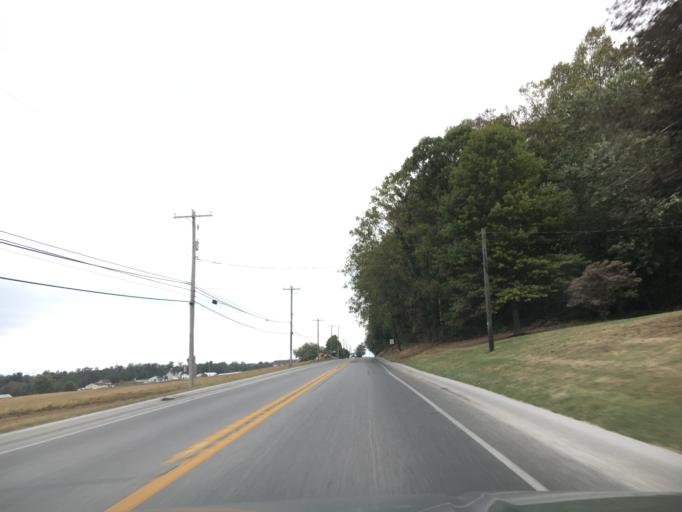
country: US
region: Pennsylvania
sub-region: Lancaster County
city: Quarryville
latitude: 39.9065
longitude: -76.1288
